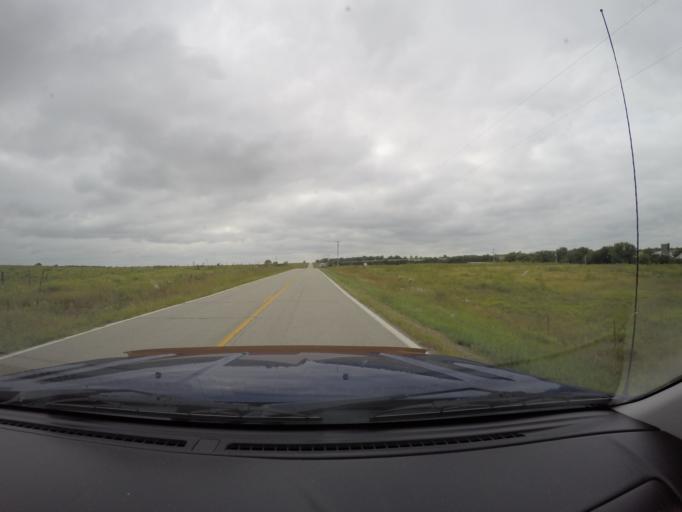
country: US
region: Kansas
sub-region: Morris County
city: Council Grove
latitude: 38.7976
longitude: -96.6413
